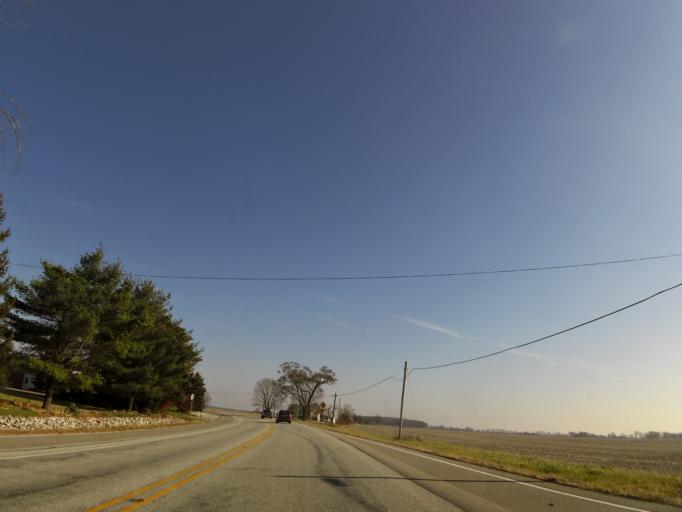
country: US
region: Indiana
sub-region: Shelby County
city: Morristown
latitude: 39.5692
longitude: -85.6217
